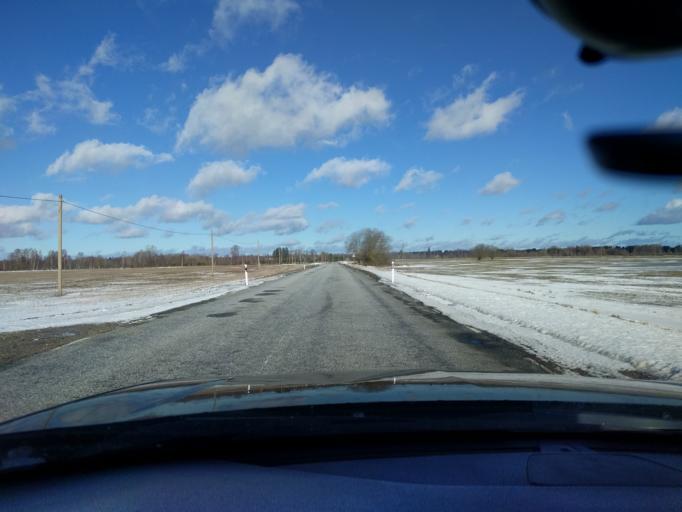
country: EE
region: Harju
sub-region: Raasiku vald
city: Raasiku
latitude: 59.3500
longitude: 25.1463
